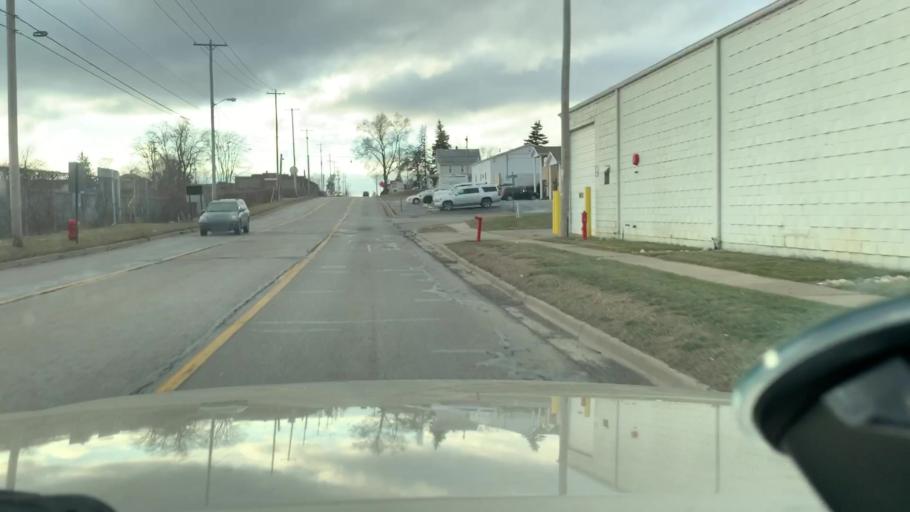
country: US
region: Michigan
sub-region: Jackson County
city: Jackson
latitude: 42.2548
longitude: -84.4326
